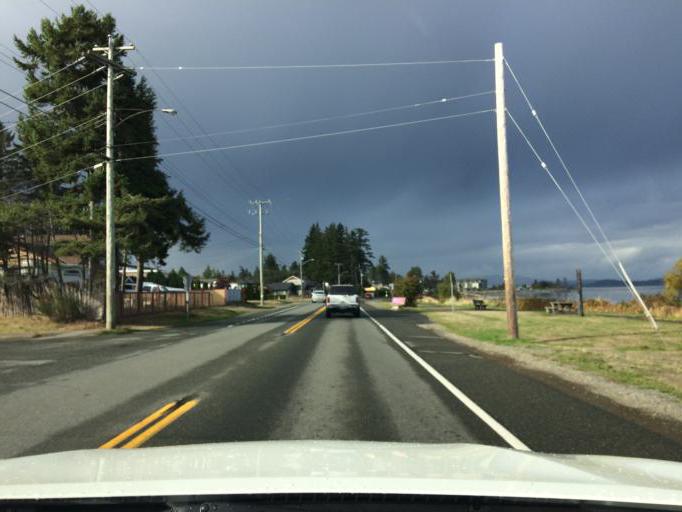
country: CA
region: British Columbia
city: Campbell River
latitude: 49.9559
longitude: -125.2056
